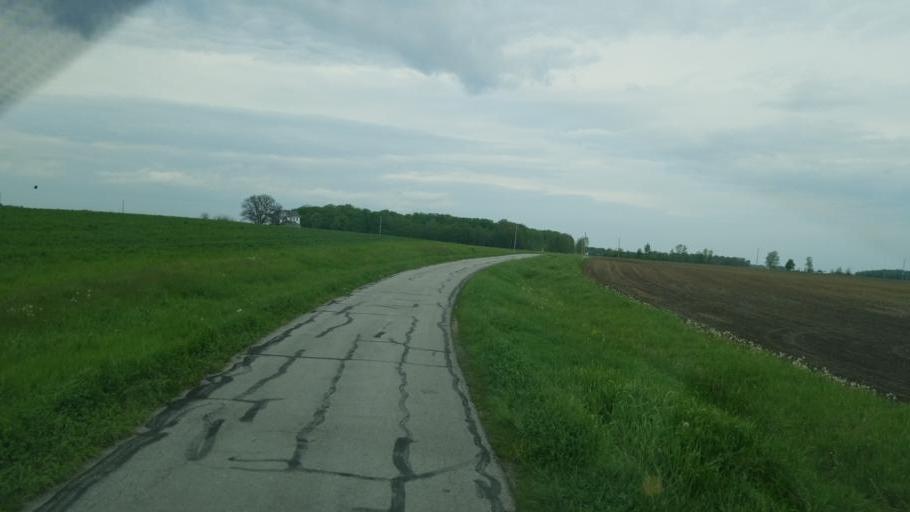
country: US
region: Ohio
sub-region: Huron County
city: Willard
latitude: 41.0170
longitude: -82.8344
